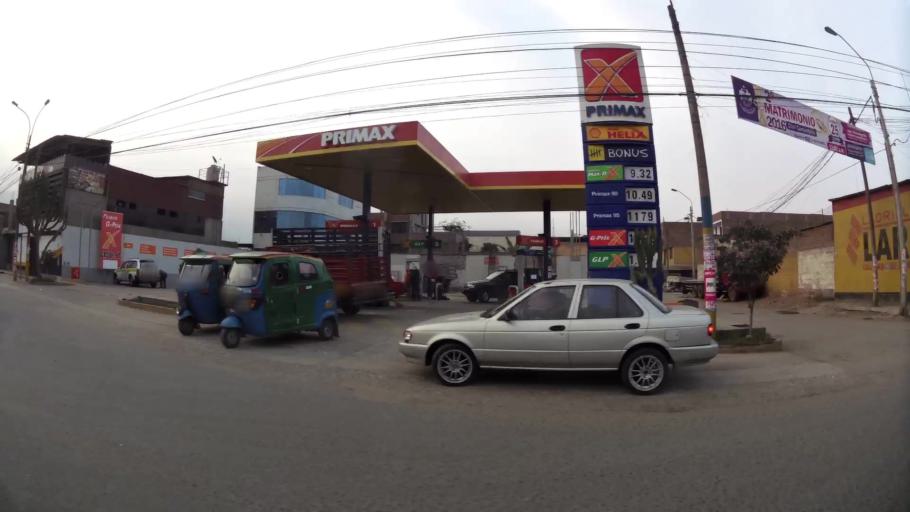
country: PE
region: Lima
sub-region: Lima
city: Independencia
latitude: -11.9857
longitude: -77.0032
